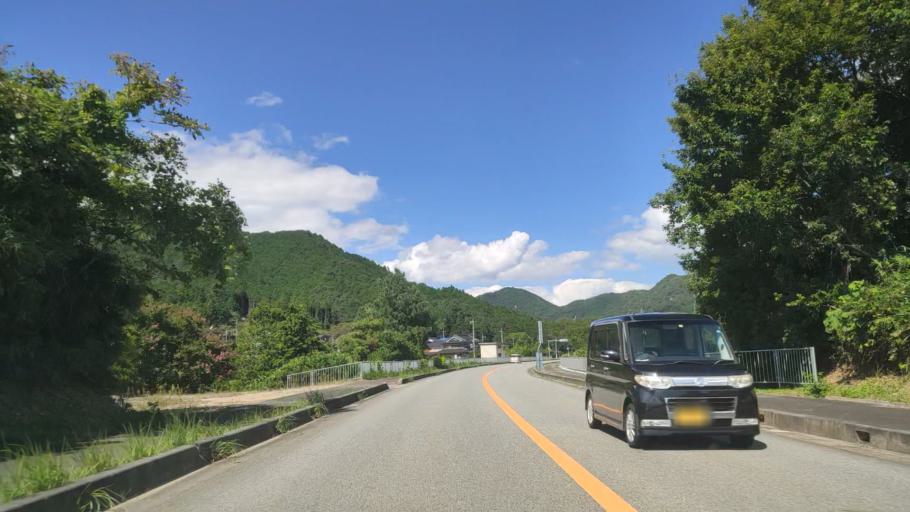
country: JP
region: Kyoto
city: Fukuchiyama
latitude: 35.2383
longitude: 135.1241
